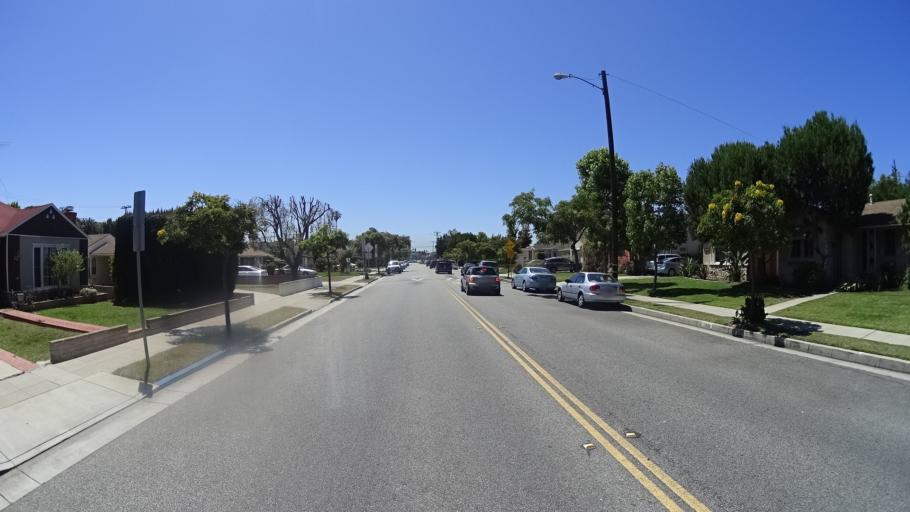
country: US
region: California
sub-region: Los Angeles County
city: Santa Monica
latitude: 34.0172
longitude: -118.4631
